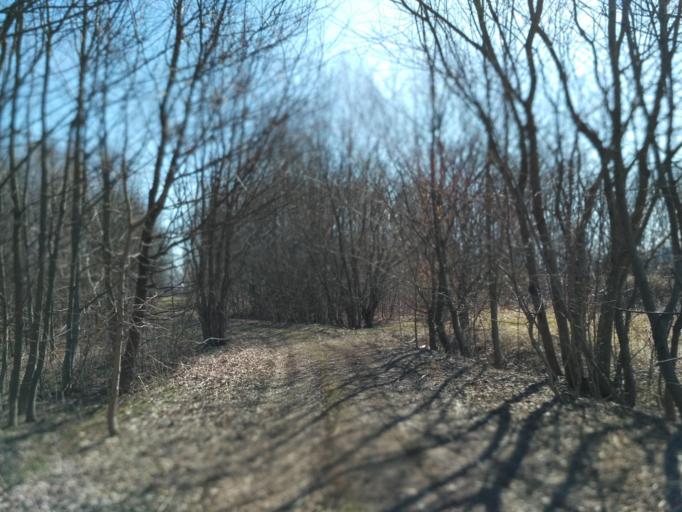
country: PL
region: Subcarpathian Voivodeship
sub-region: Powiat brzozowski
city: Domaradz
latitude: 49.7981
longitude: 21.9685
